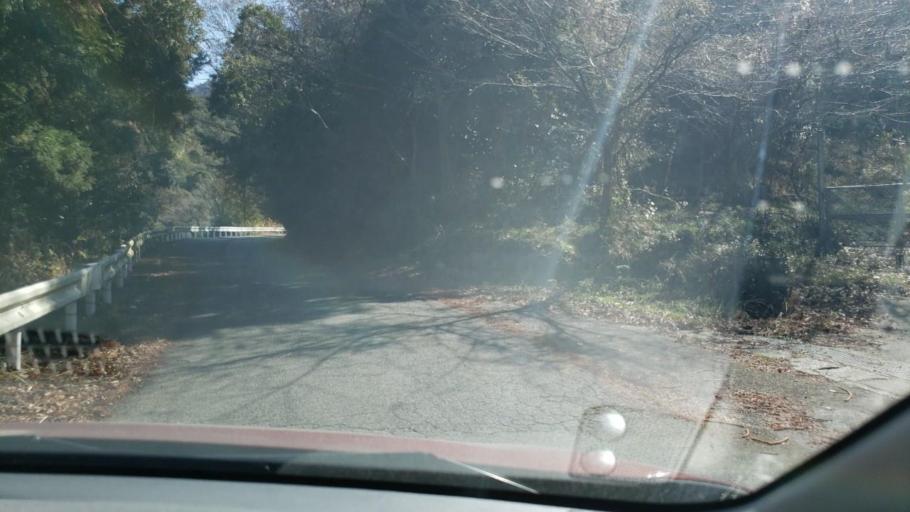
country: JP
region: Tokushima
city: Narutocho-mitsuishi
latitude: 34.2033
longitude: 134.5529
